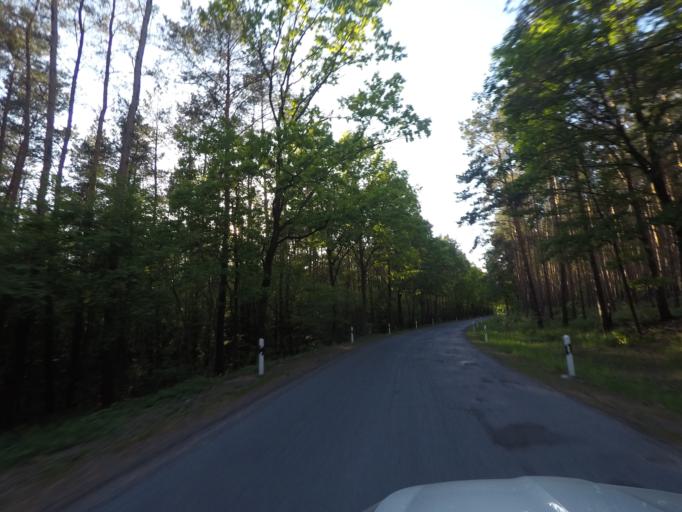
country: DE
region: Brandenburg
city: Bad Freienwalde
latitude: 52.8182
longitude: 14.0163
